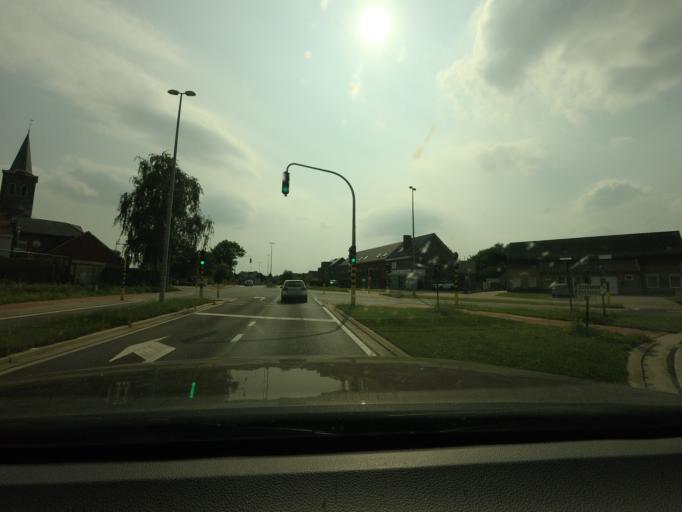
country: BE
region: Flanders
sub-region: Provincie Limburg
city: Beringen
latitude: 51.0880
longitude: 5.2193
